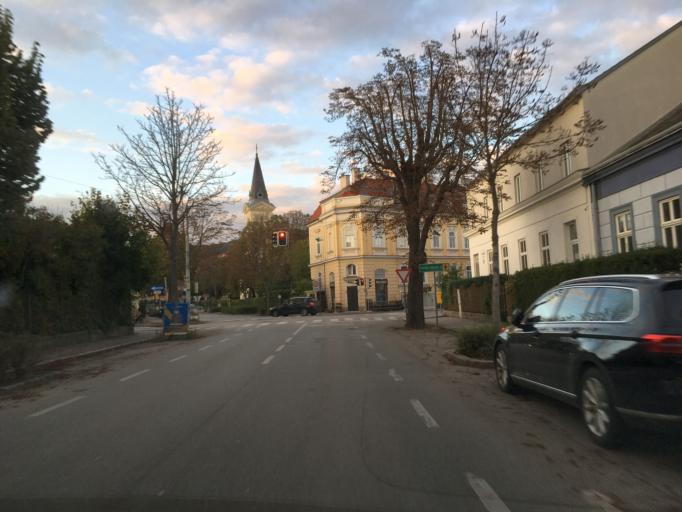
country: AT
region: Lower Austria
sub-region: Politischer Bezirk Baden
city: Baden
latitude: 48.0105
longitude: 16.2438
